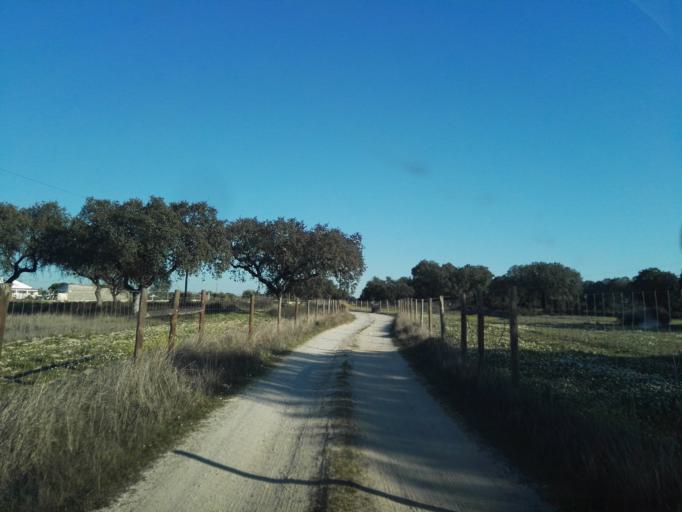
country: PT
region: Evora
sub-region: Evora
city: Evora
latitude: 38.5455
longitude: -7.9509
